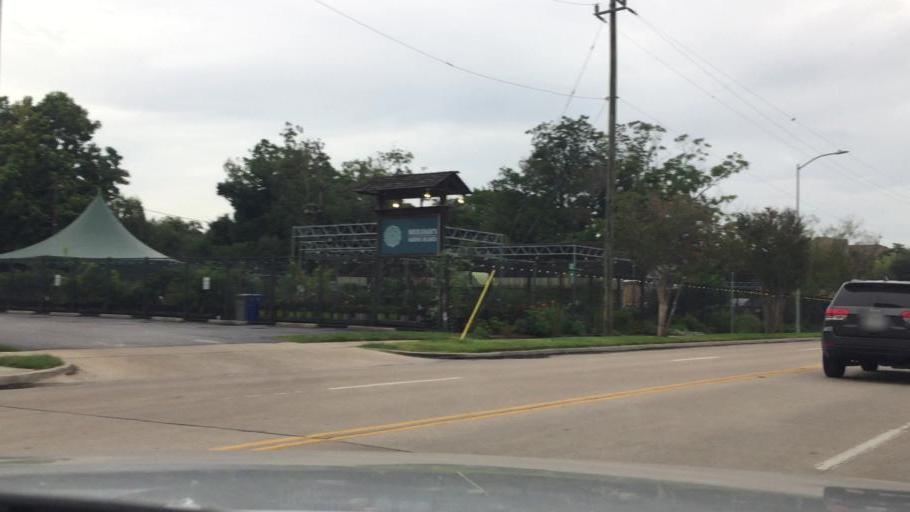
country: US
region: Texas
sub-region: Harris County
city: Houston
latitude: 29.7907
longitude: -95.3920
